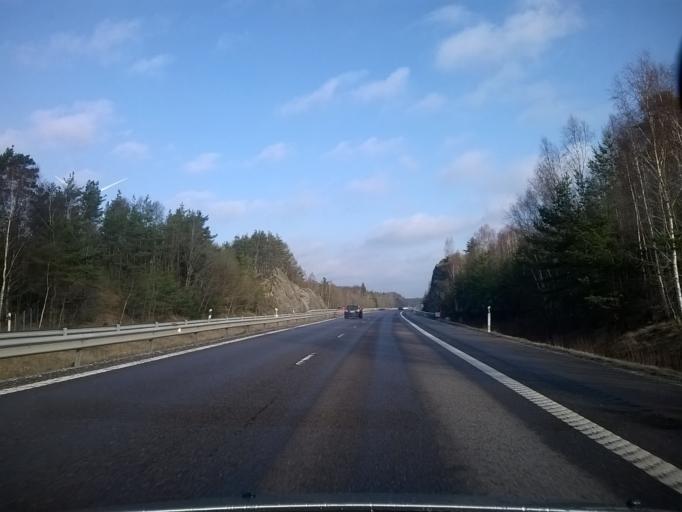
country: SE
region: Vaestra Goetaland
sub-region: Kungalvs Kommun
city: Kode
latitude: 57.9213
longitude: 11.8807
